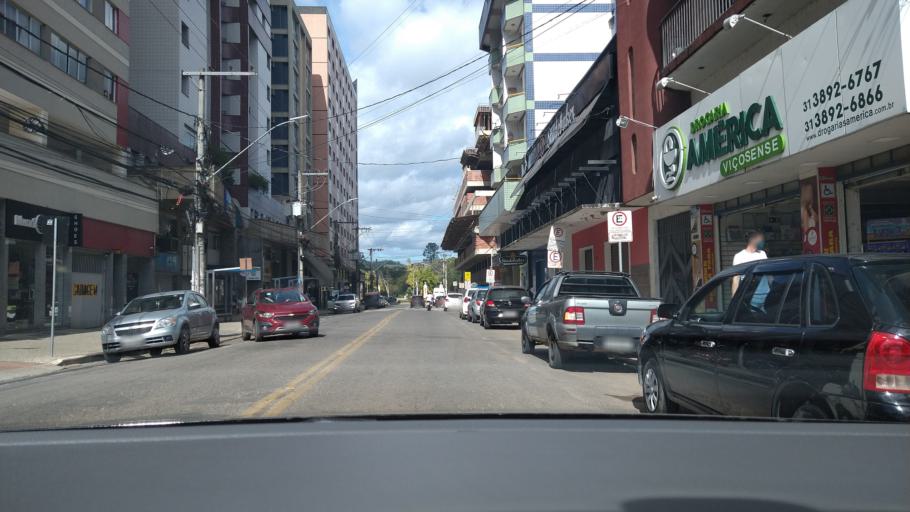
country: BR
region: Minas Gerais
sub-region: Vicosa
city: Vicosa
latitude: -20.7565
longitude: -42.8765
